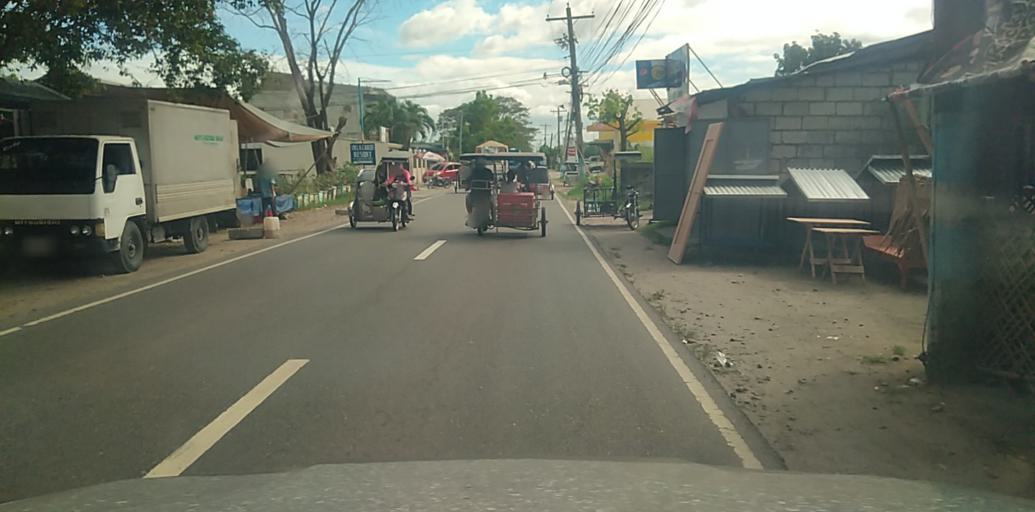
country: PH
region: Central Luzon
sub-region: Province of Pampanga
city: Arenas
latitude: 15.1772
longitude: 120.6788
